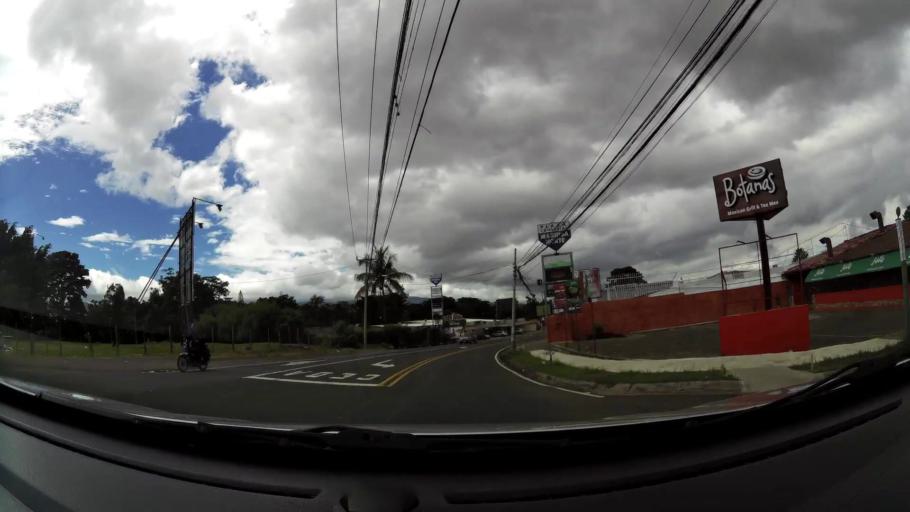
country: CR
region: San Jose
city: Curridabat
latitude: 9.9118
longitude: -84.0200
